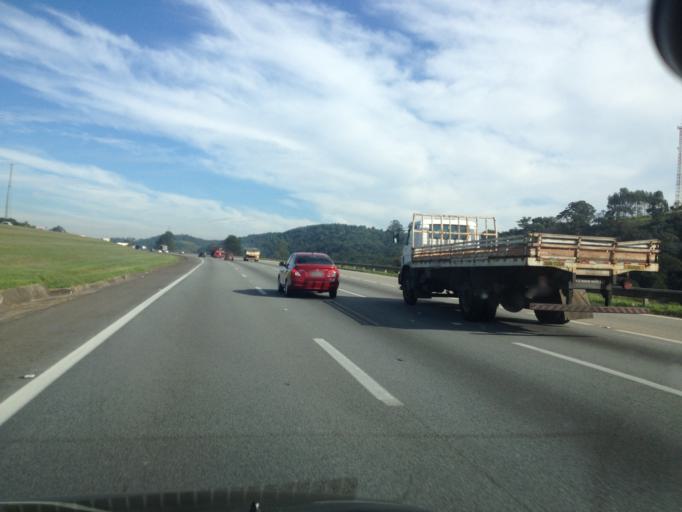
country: BR
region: Sao Paulo
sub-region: Mairinque
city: Mairinque
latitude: -23.4183
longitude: -47.2149
